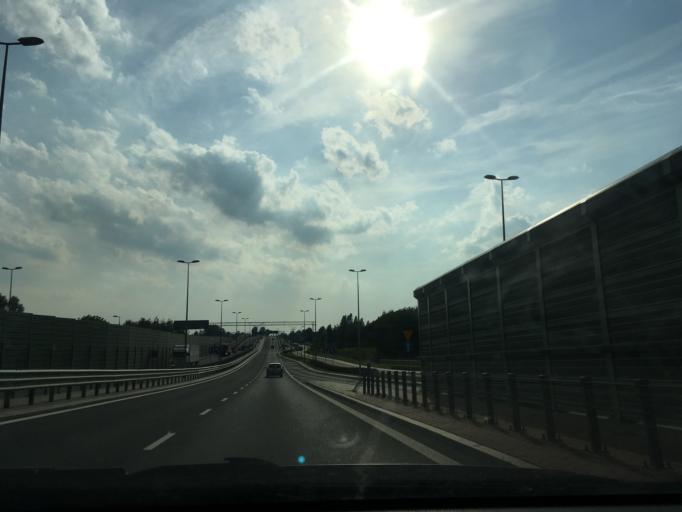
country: PL
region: Podlasie
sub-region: Bialystok
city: Bialystok
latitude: 53.1554
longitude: 23.0846
